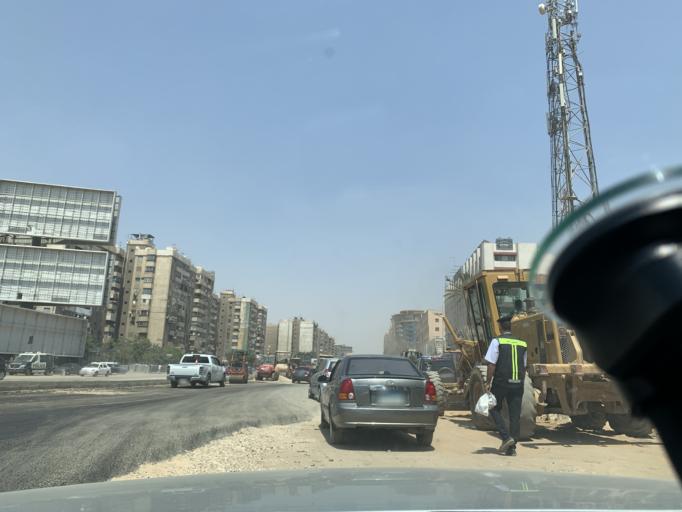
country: EG
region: Muhafazat al Qahirah
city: Cairo
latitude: 30.0690
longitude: 31.3407
